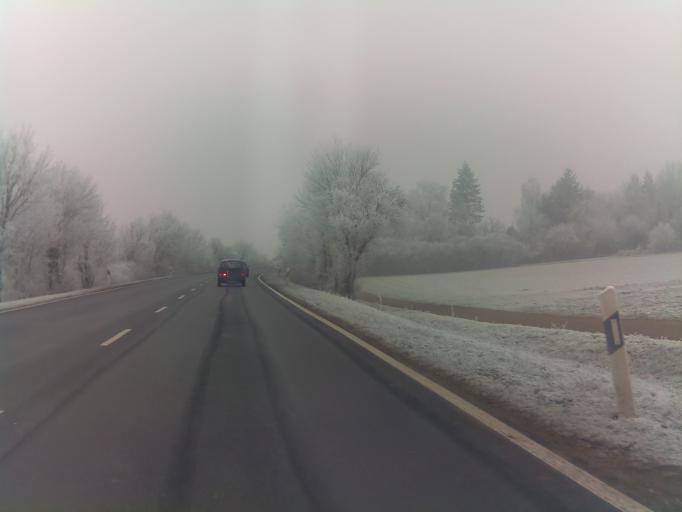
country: DE
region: Bavaria
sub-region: Regierungsbezirk Unterfranken
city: Hassfurt
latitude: 50.0454
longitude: 10.5219
